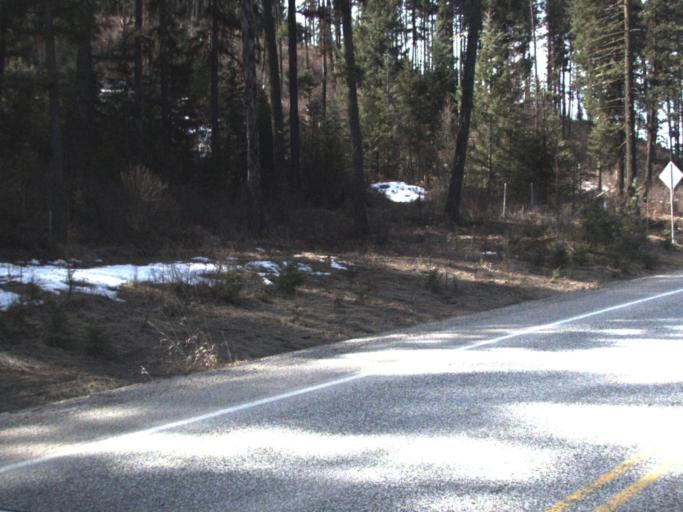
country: US
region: Washington
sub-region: Stevens County
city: Colville
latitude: 48.5154
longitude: -117.7574
